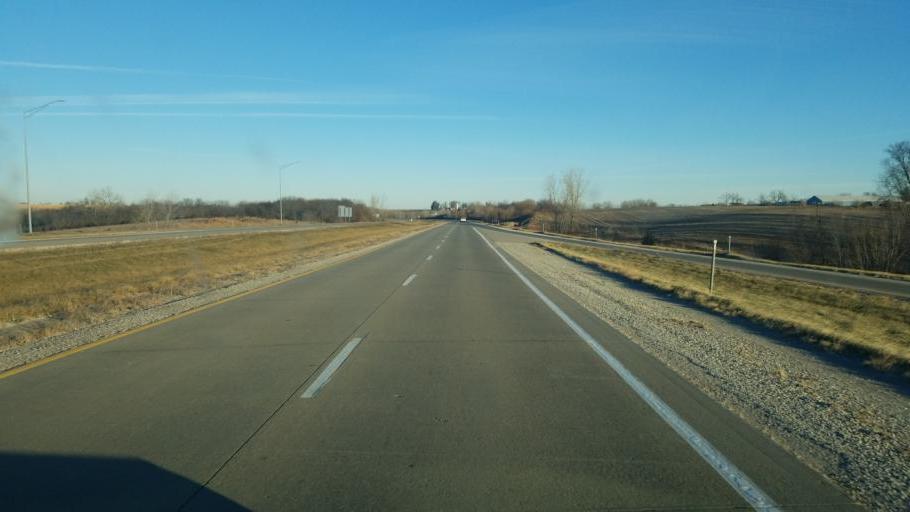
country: US
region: Iowa
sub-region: Mahaska County
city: Oskaloosa
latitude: 41.2998
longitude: -92.6746
